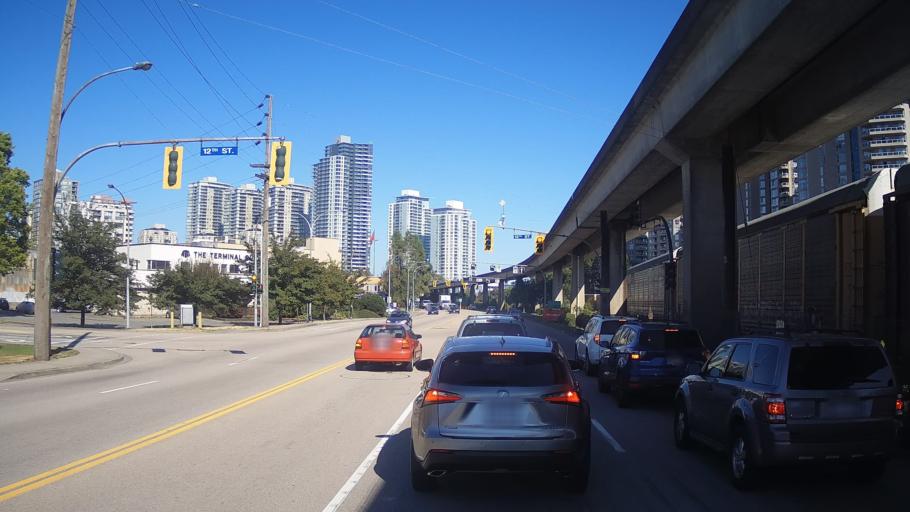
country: CA
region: British Columbia
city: New Westminster
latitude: 49.2012
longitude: -122.9227
